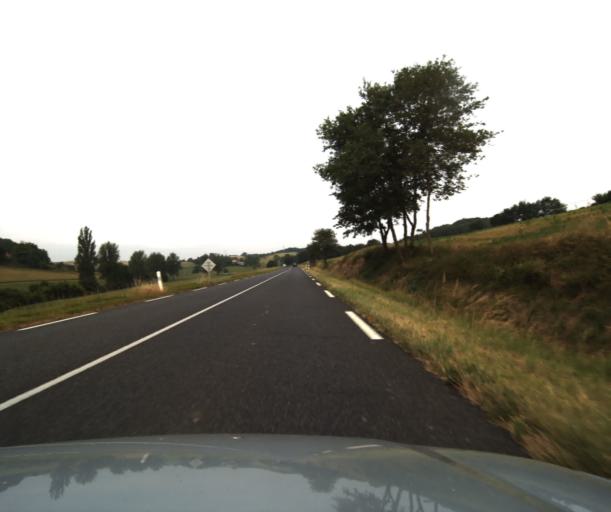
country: FR
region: Midi-Pyrenees
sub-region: Departement du Gers
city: Pavie
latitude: 43.5625
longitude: 0.5079
